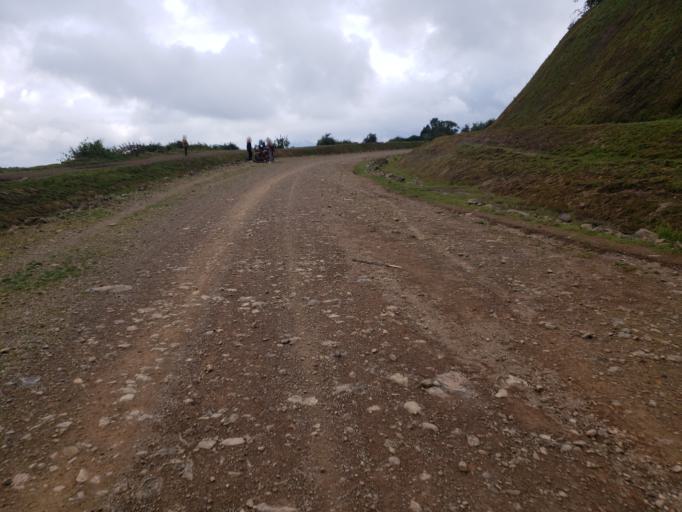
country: ET
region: Oromiya
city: Dodola
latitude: 6.6940
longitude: 39.3694
